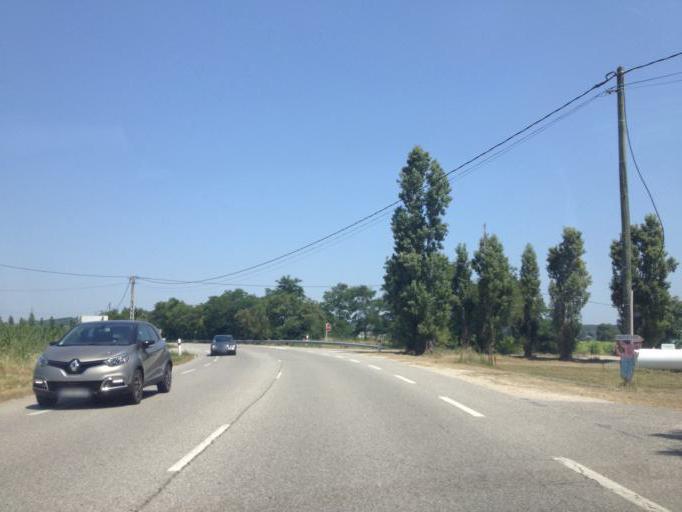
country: FR
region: Rhone-Alpes
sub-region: Departement de la Drome
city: Beaumont-Monteux
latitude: 45.0360
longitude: 4.9319
